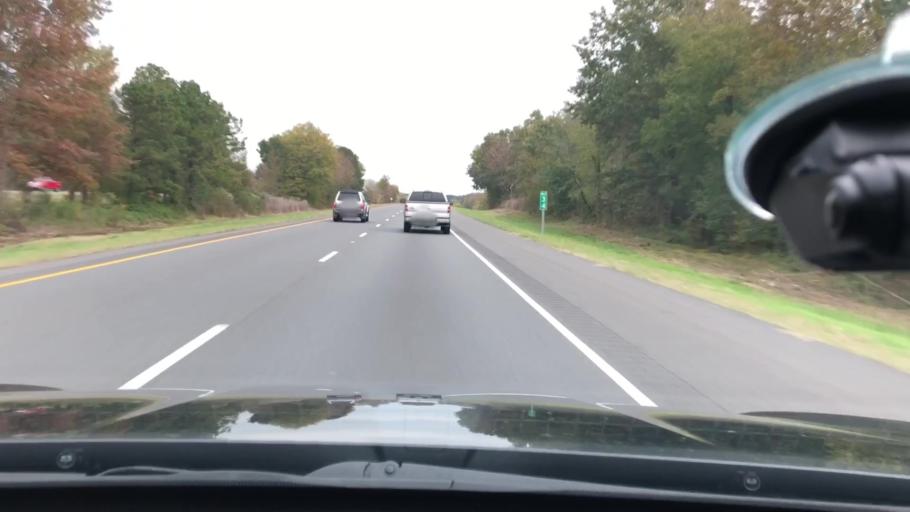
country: US
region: Arkansas
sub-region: Hempstead County
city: Hope
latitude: 33.7198
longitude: -93.5571
